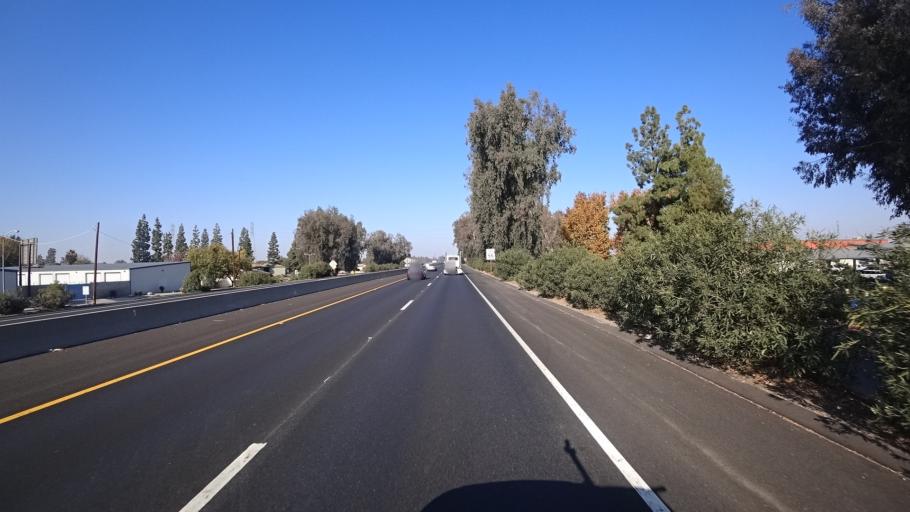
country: US
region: California
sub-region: Kern County
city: Bakersfield
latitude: 35.3914
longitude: -119.0254
